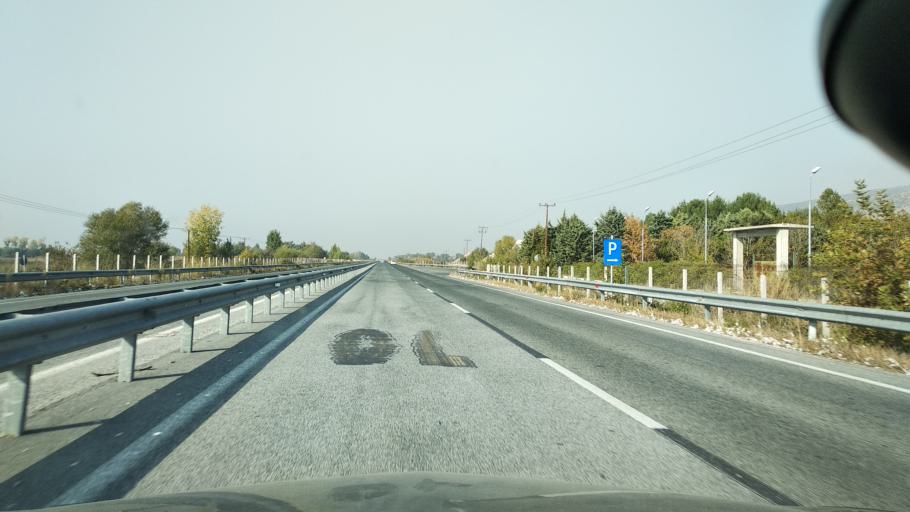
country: GR
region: Thessaly
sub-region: Trikala
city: Oichalia
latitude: 39.5640
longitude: 21.9643
